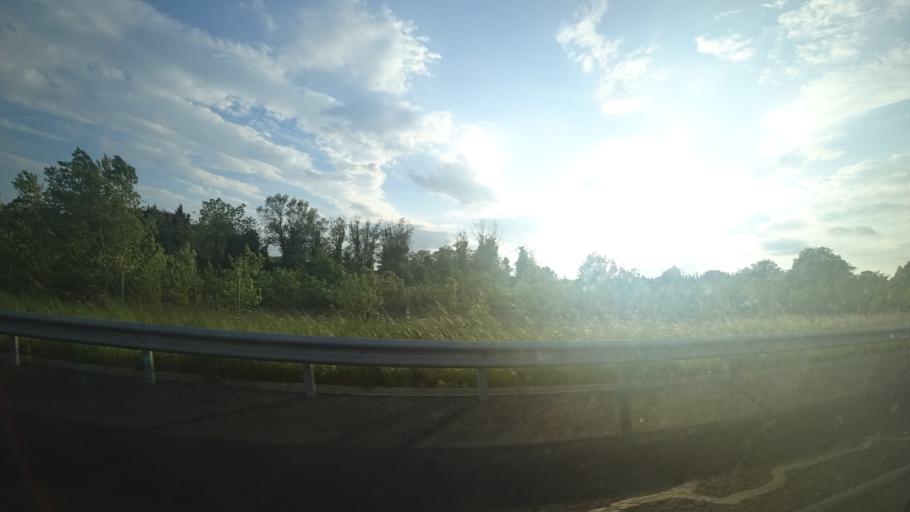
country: FR
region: Languedoc-Roussillon
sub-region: Departement de l'Herault
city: Nebian
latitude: 43.6000
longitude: 3.4618
